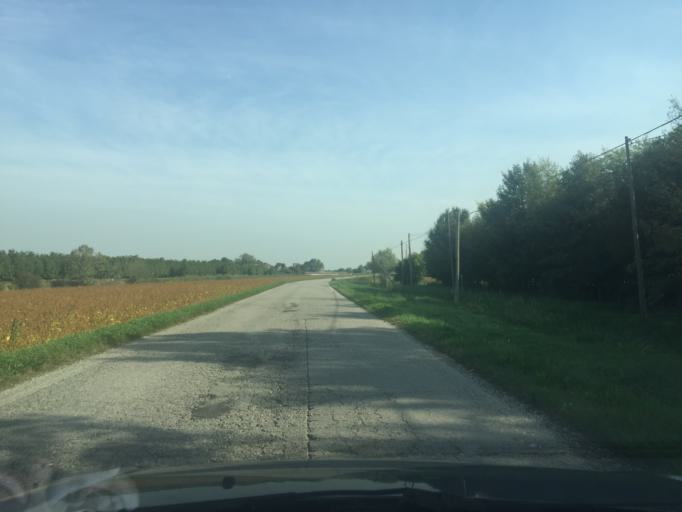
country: IT
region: Veneto
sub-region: Provincia di Venezia
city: Ceggia
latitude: 45.6324
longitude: 12.6521
